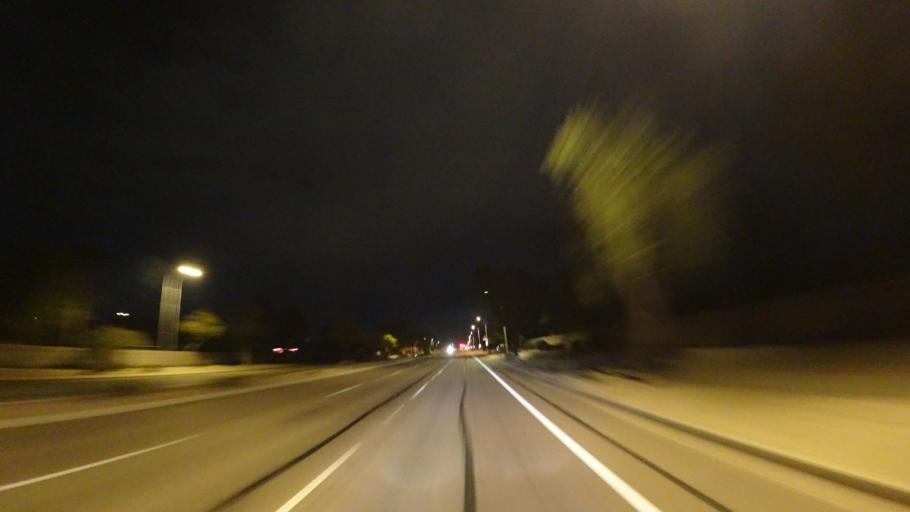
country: US
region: Arizona
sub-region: Maricopa County
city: Chandler
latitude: 33.2913
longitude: -111.8669
